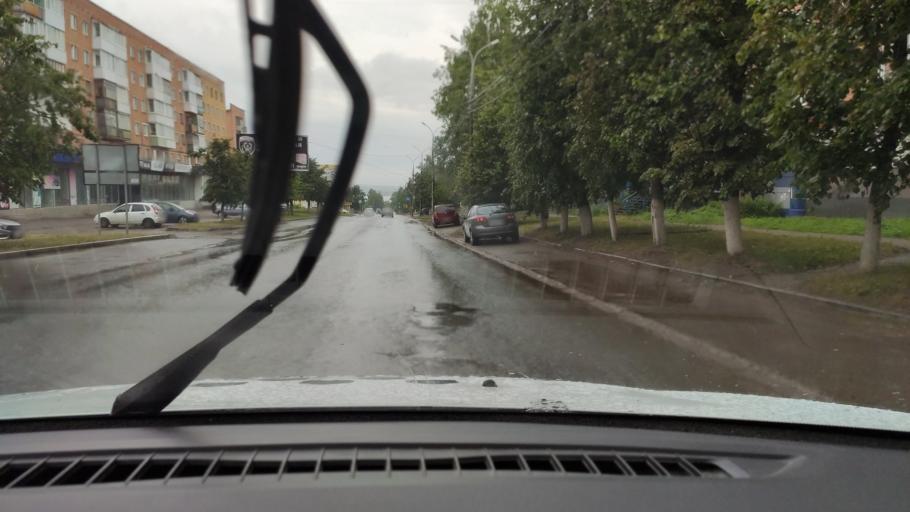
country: RU
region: Udmurtiya
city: Votkinsk
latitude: 57.0623
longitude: 53.9972
